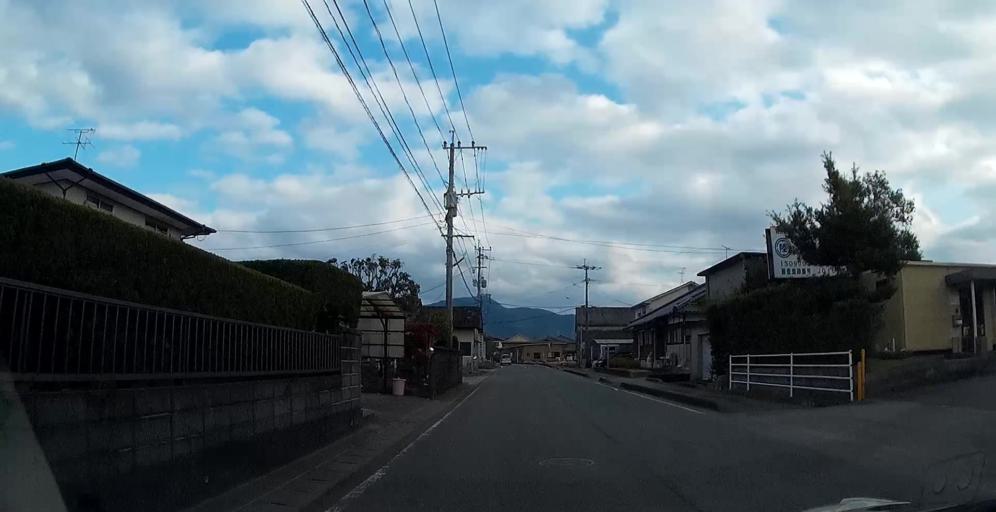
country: JP
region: Kumamoto
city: Yatsushiro
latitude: 32.5392
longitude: 130.6268
